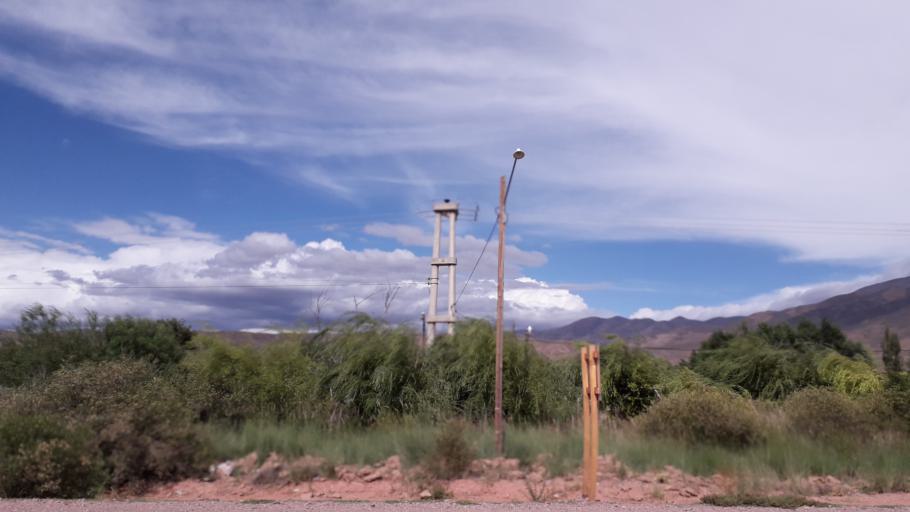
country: AR
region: Jujuy
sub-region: Departamento de Humahuaca
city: Humahuaca
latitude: -23.3070
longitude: -65.3541
